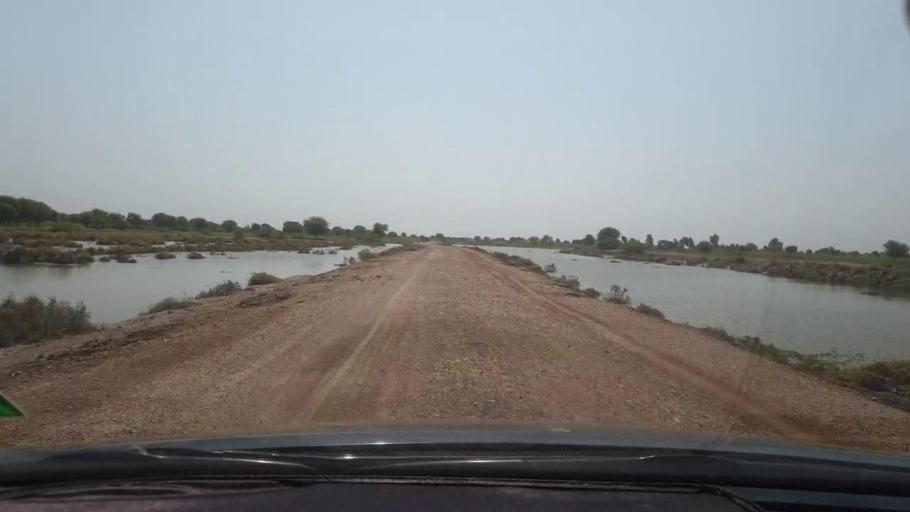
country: PK
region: Sindh
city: Tando Bago
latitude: 24.8106
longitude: 69.1655
